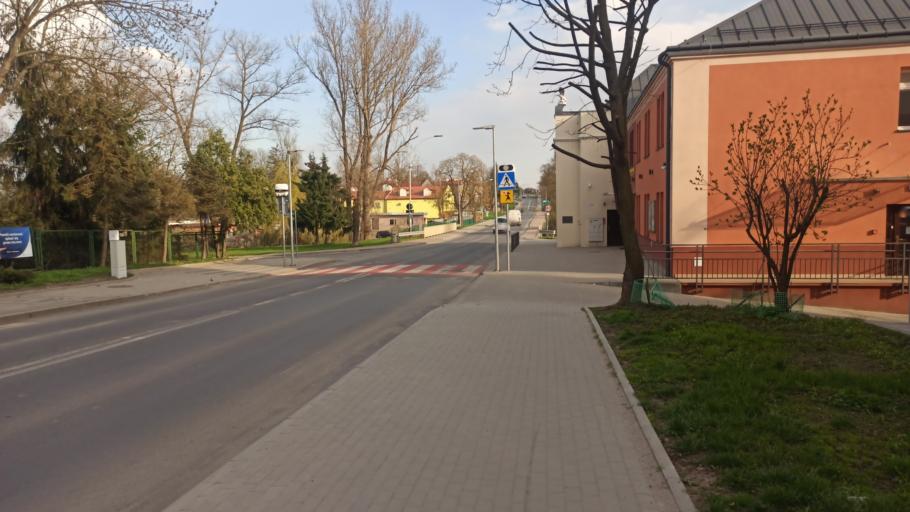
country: PL
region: Subcarpathian Voivodeship
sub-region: Powiat jaroslawski
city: Radymno
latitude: 49.9505
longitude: 22.8204
